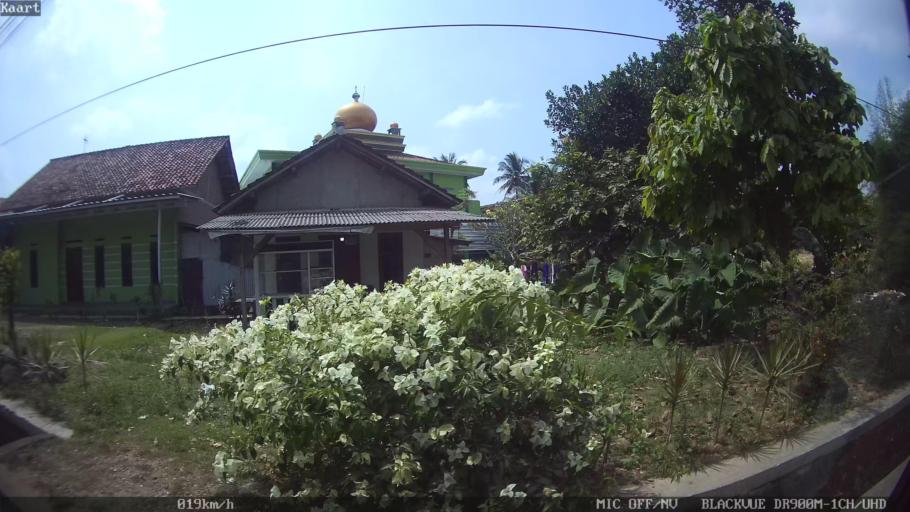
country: ID
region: Lampung
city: Pringsewu
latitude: -5.3654
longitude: 104.9721
